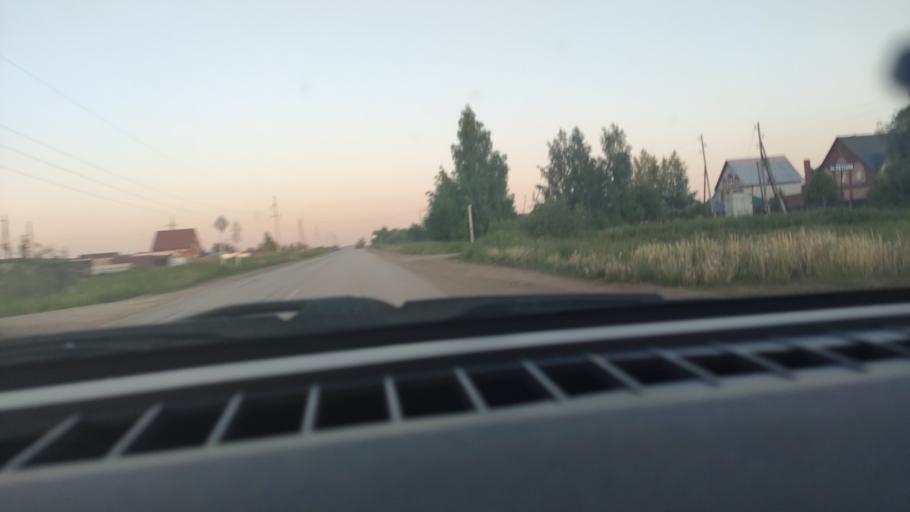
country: RU
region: Perm
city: Kultayevo
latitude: 57.8927
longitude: 55.9172
